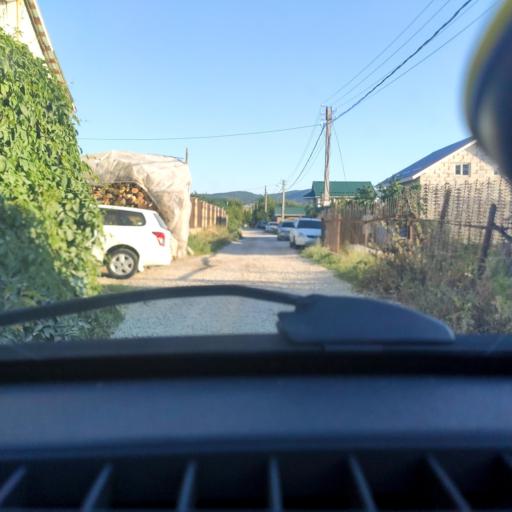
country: RU
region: Samara
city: Zhigulevsk
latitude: 53.4668
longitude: 49.5924
